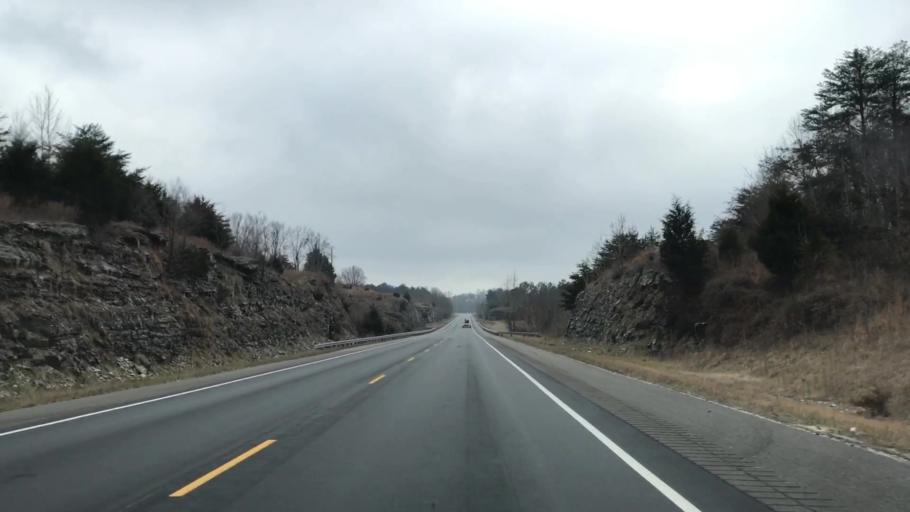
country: US
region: Kentucky
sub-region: Metcalfe County
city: Edmonton
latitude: 36.9497
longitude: -85.4459
